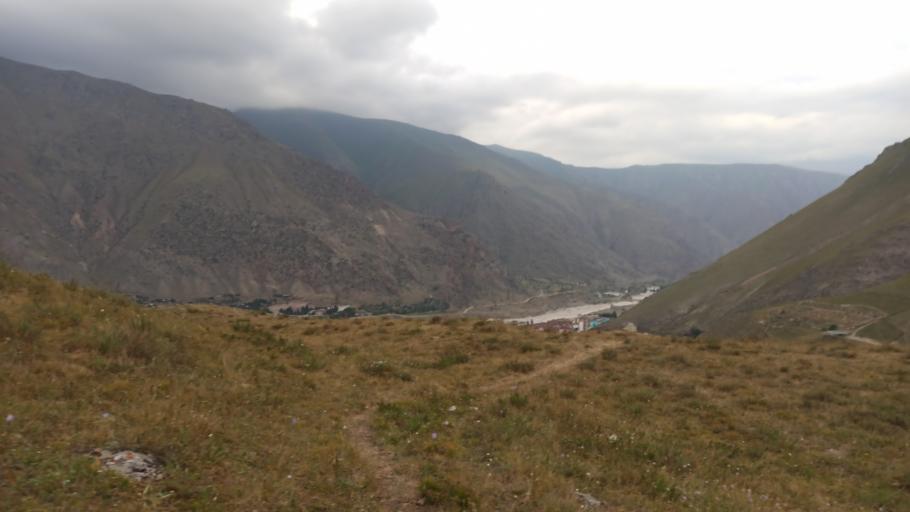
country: RU
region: Kabardino-Balkariya
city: Tyrnyauz
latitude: 43.3914
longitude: 42.9268
